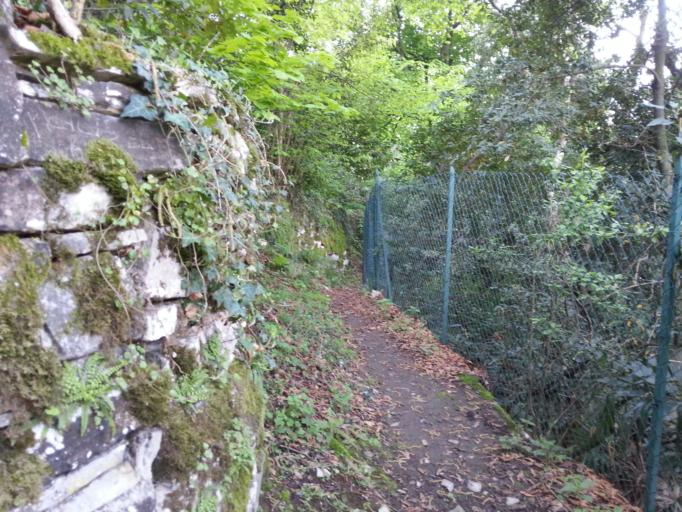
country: IT
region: Lombardy
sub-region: Provincia di Como
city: Torno
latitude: 45.8545
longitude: 9.1154
